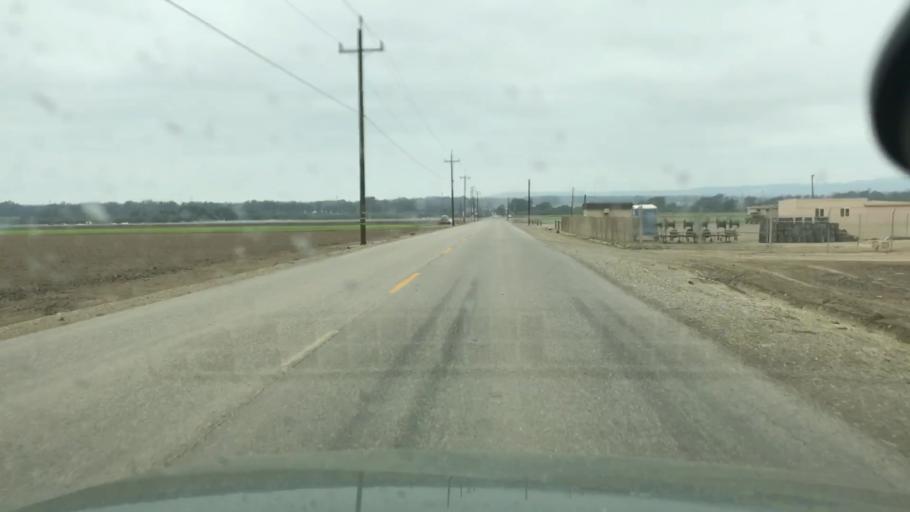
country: US
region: California
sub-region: Santa Barbara County
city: Lompoc
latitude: 34.6540
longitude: -120.4929
